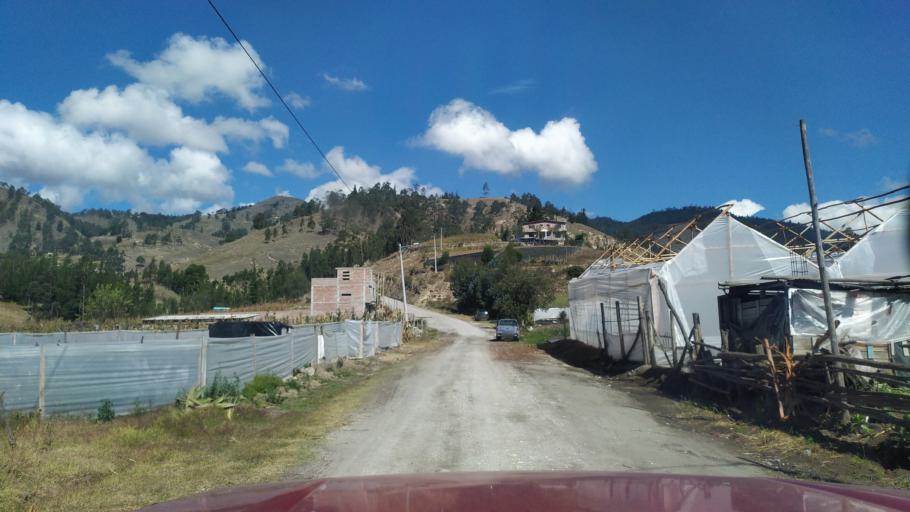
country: EC
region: Chimborazo
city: Riobamba
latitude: -1.6808
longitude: -78.6899
